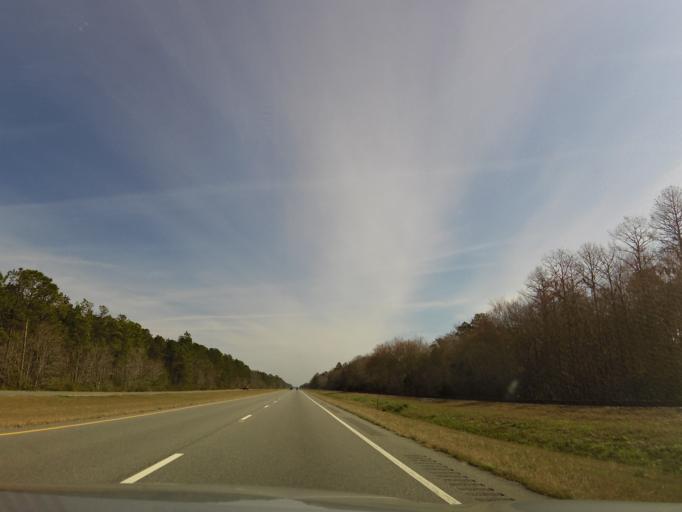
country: US
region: Georgia
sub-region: Lowndes County
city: Valdosta
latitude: 30.8796
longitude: -83.1516
